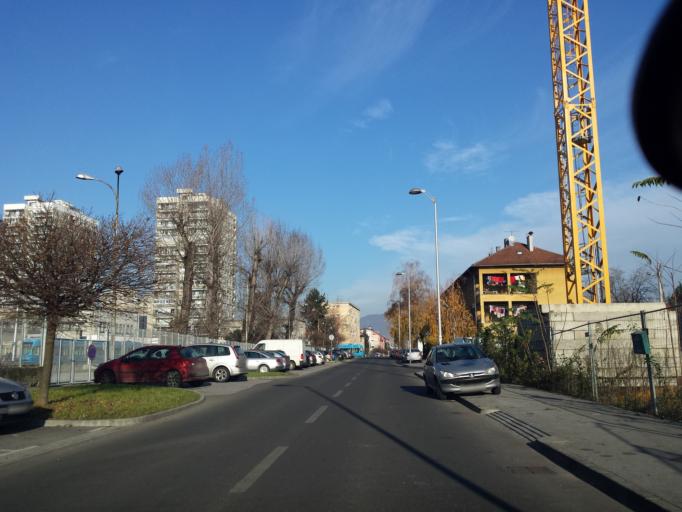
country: HR
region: Grad Zagreb
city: Jankomir
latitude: 45.7960
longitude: 15.9401
